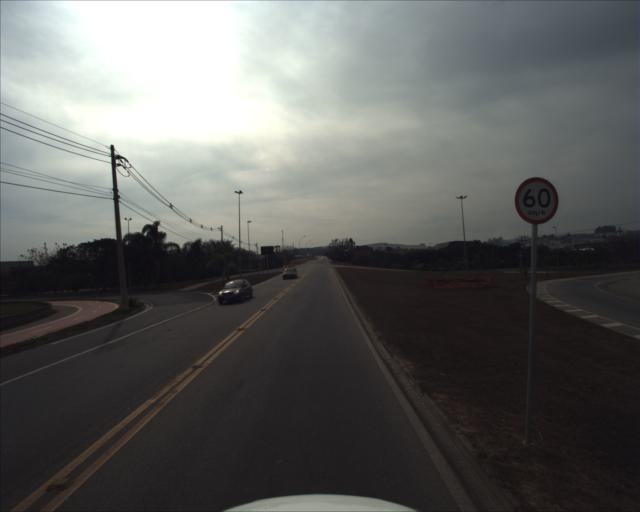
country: BR
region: Sao Paulo
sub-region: Sorocaba
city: Sorocaba
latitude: -23.4703
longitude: -47.4539
